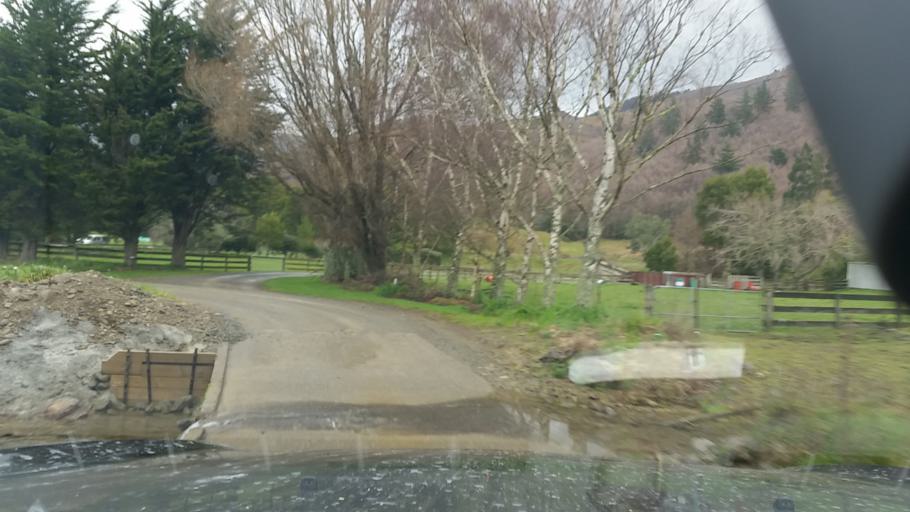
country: NZ
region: Marlborough
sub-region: Marlborough District
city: Picton
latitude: -41.3031
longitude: 173.6632
